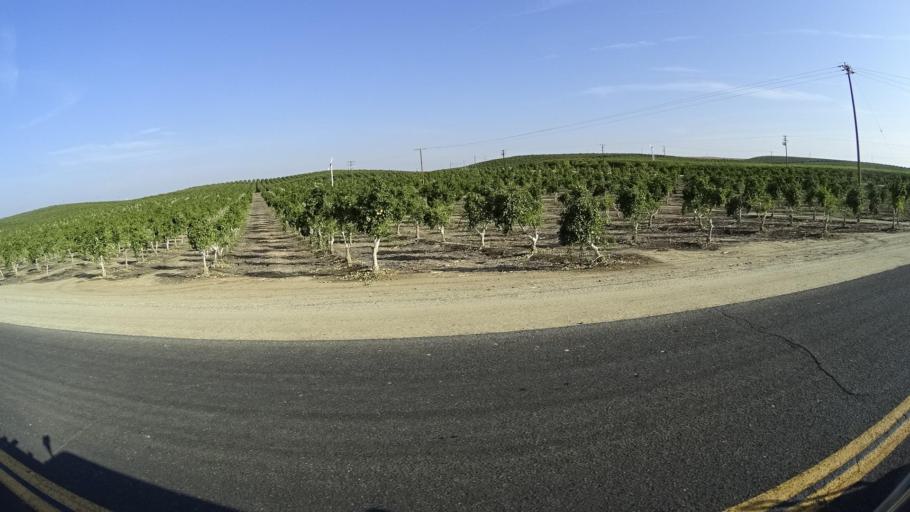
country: US
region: California
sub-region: Tulare County
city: Richgrove
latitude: 35.6616
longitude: -119.0870
